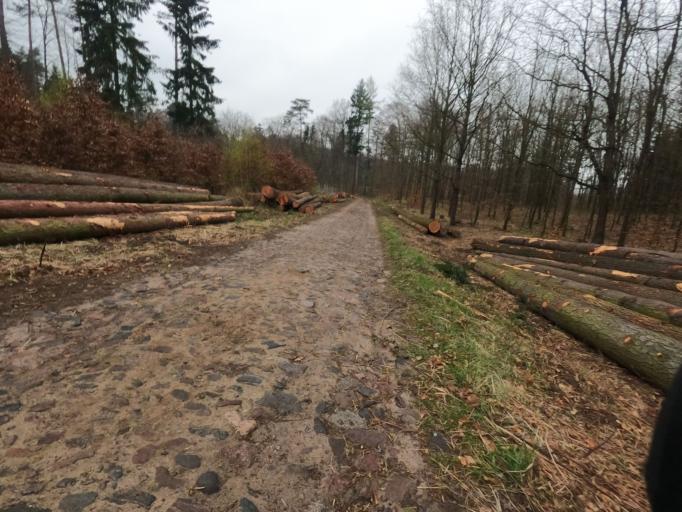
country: PL
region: West Pomeranian Voivodeship
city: Trzcinsko Zdroj
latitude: 52.9270
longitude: 14.6992
